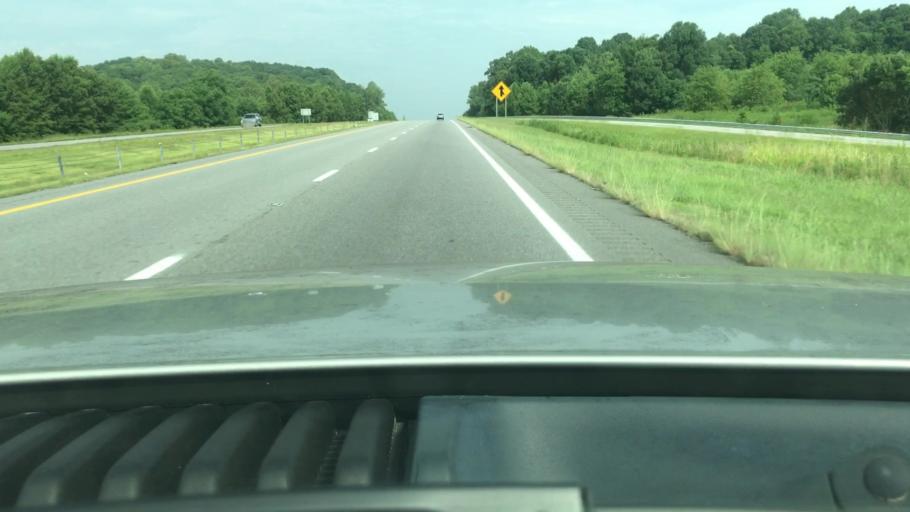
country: US
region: North Carolina
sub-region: Yadkin County
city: Jonesville
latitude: 36.1550
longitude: -80.9320
